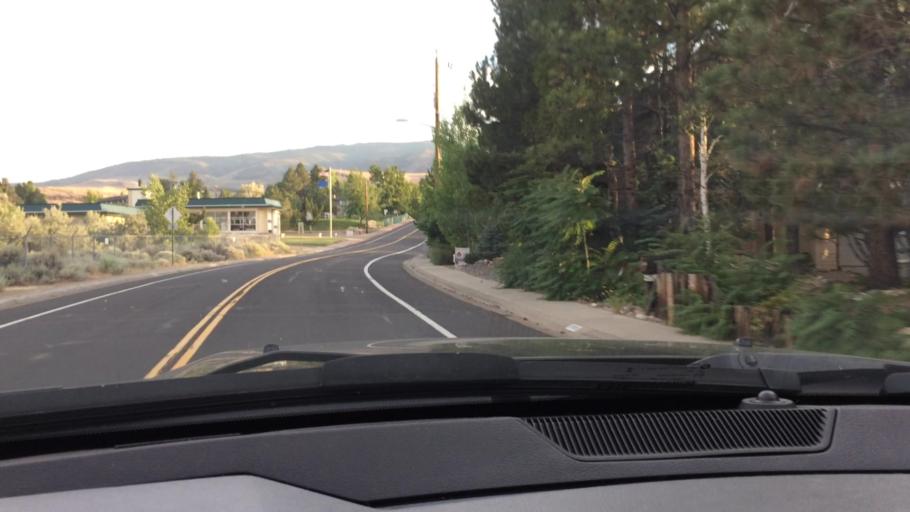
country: US
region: Nevada
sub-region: Washoe County
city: Reno
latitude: 39.4839
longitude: -119.8338
